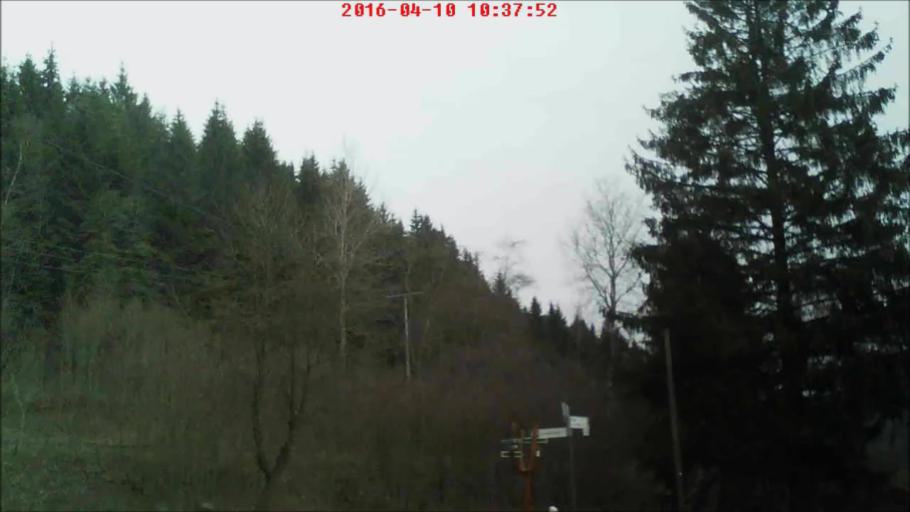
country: DE
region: Thuringia
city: Stutzerbach
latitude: 50.6226
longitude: 10.8551
